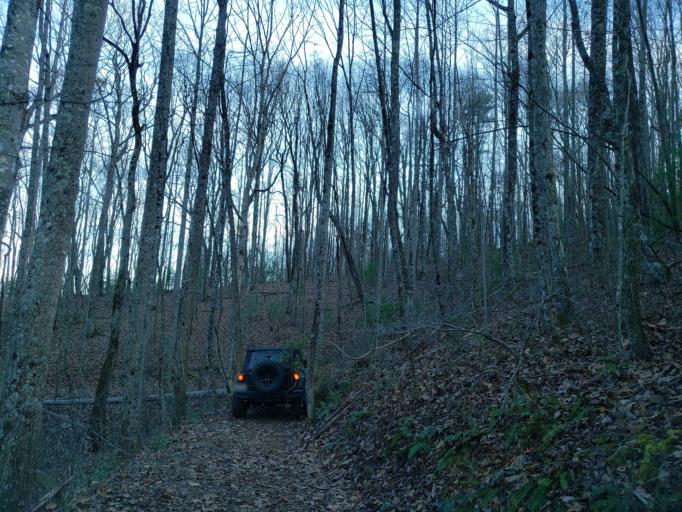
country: US
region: Georgia
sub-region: Lumpkin County
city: Dahlonega
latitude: 34.6681
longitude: -84.1008
